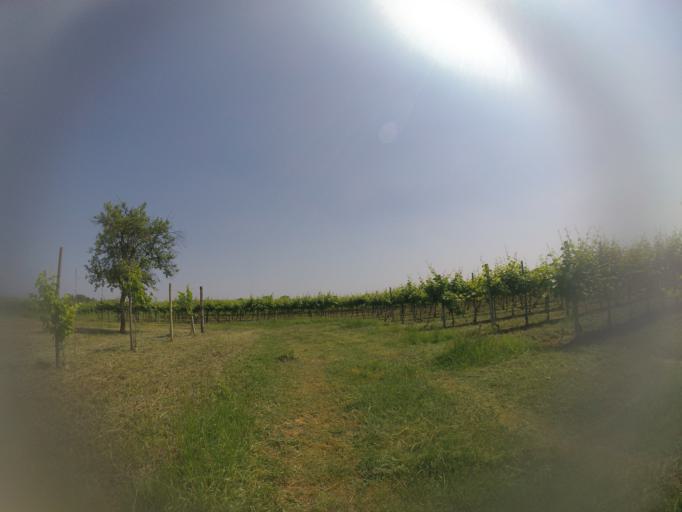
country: IT
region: Friuli Venezia Giulia
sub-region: Provincia di Udine
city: Bertiolo
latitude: 45.9385
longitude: 13.0448
